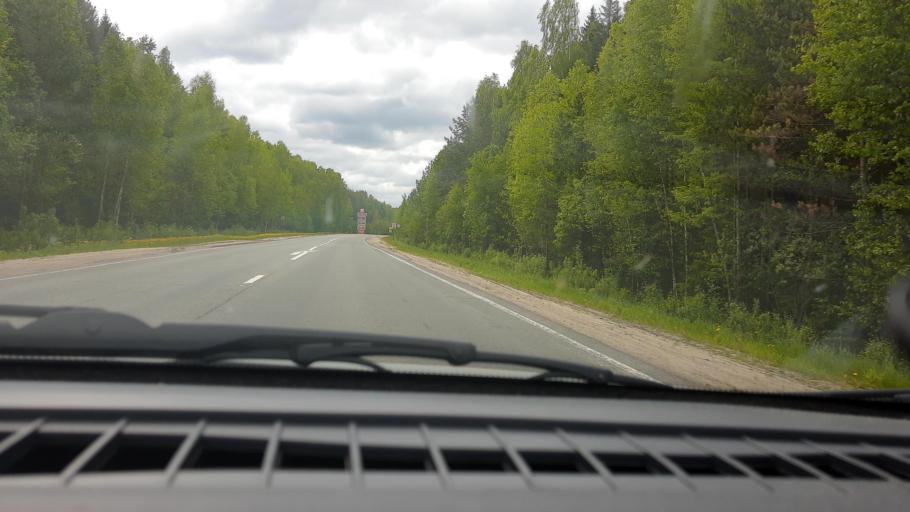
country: RU
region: Nizjnij Novgorod
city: Semenov
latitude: 56.7685
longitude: 44.4125
